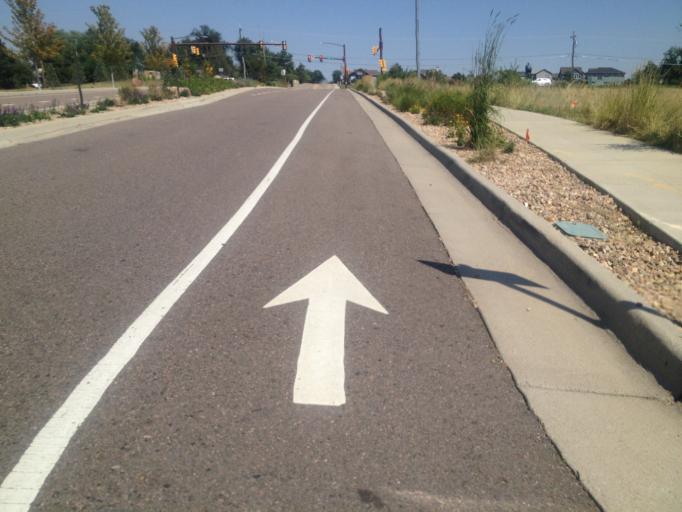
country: US
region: Colorado
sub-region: Boulder County
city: Louisville
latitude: 39.9941
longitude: -105.1292
